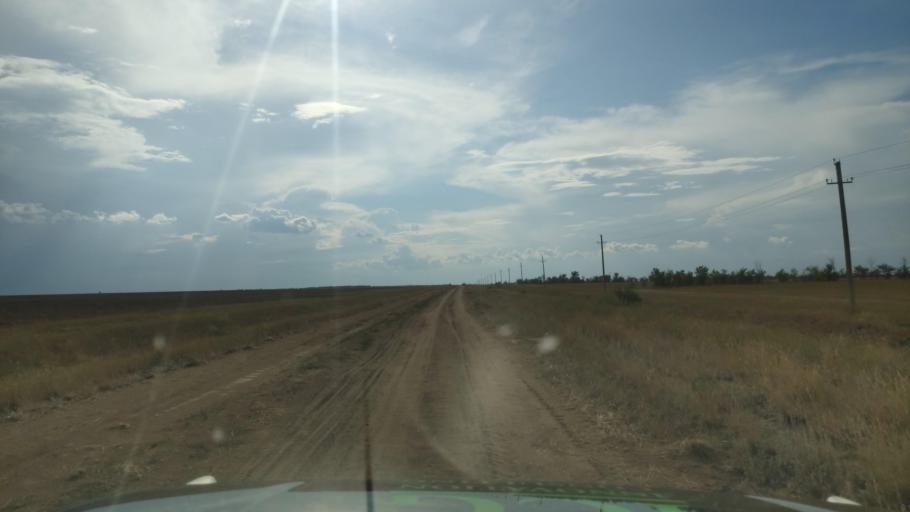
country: KZ
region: Pavlodar
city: Pavlodar
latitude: 52.5125
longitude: 77.4812
